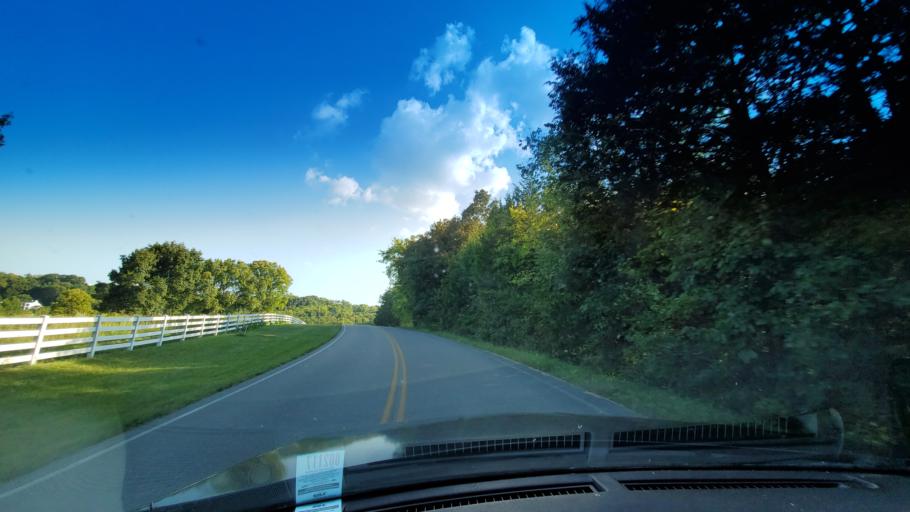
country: US
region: Tennessee
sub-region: Wilson County
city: Lebanon
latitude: 36.1637
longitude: -86.3739
